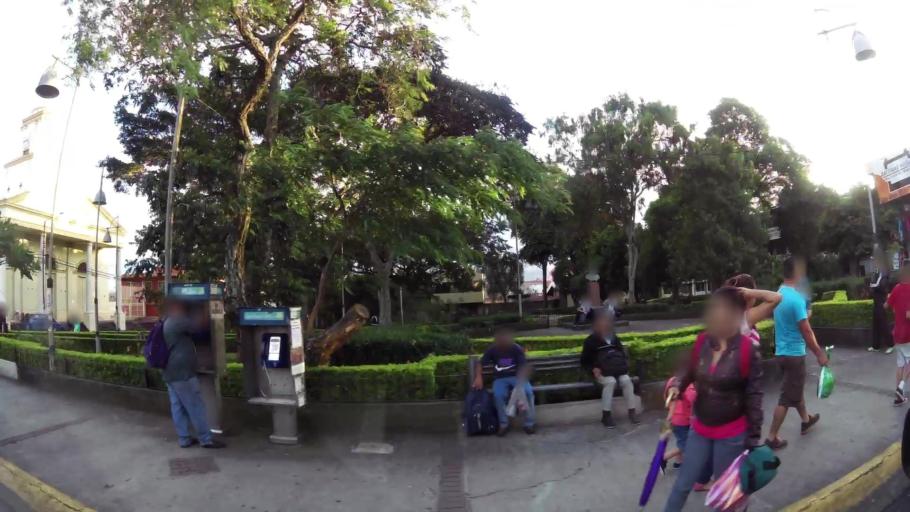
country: CR
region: Heredia
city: Heredia
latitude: 9.9970
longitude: -84.1153
